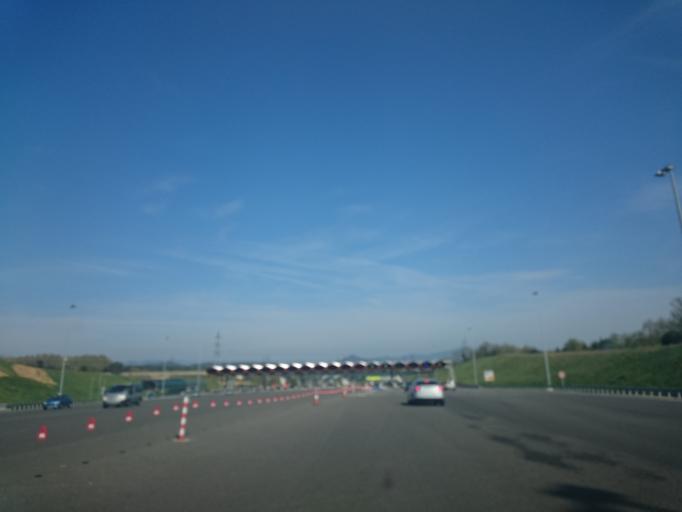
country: ES
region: Catalonia
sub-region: Provincia de Girona
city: Fornells de la Selva
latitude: 41.9274
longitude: 2.7919
